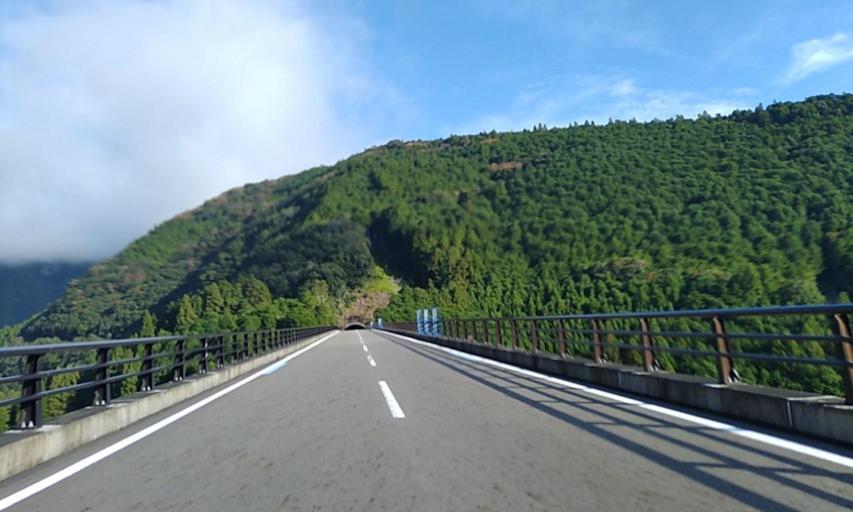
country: JP
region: Wakayama
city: Shingu
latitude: 33.8932
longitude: 135.8797
